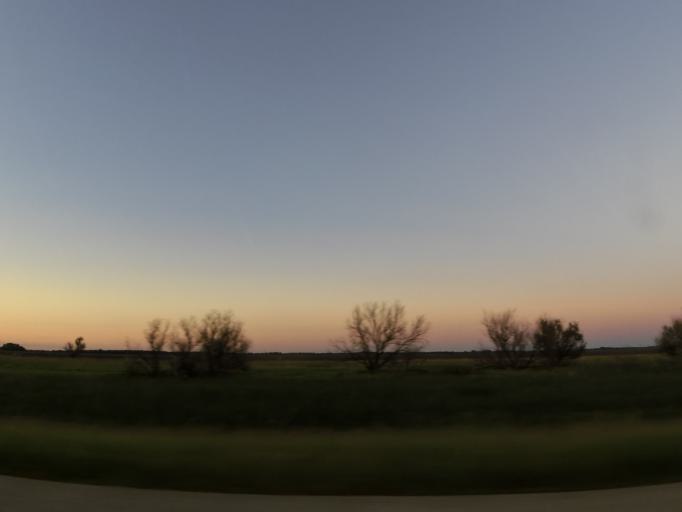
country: US
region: North Dakota
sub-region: Grand Forks County
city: Grand Forks
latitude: 48.0502
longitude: -97.1515
